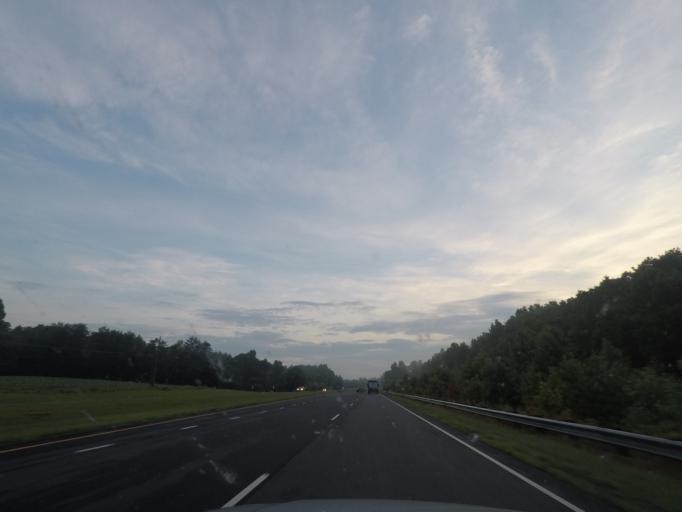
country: US
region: North Carolina
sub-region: Person County
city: Roxboro
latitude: 36.2589
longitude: -78.9438
